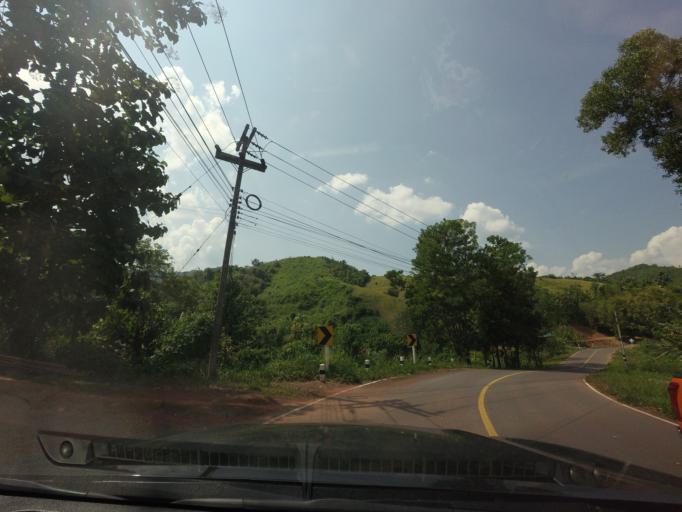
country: TH
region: Nan
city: Bo Kluea
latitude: 19.0133
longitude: 101.1919
